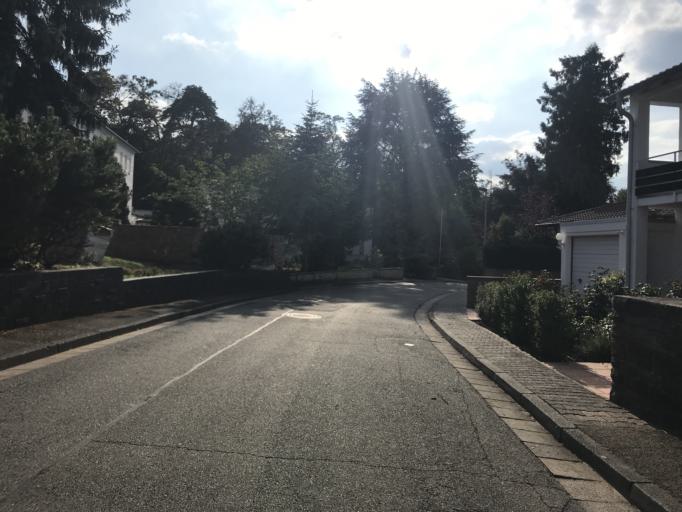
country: DE
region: Rheinland-Pfalz
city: Budenheim
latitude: 50.0178
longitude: 8.1757
